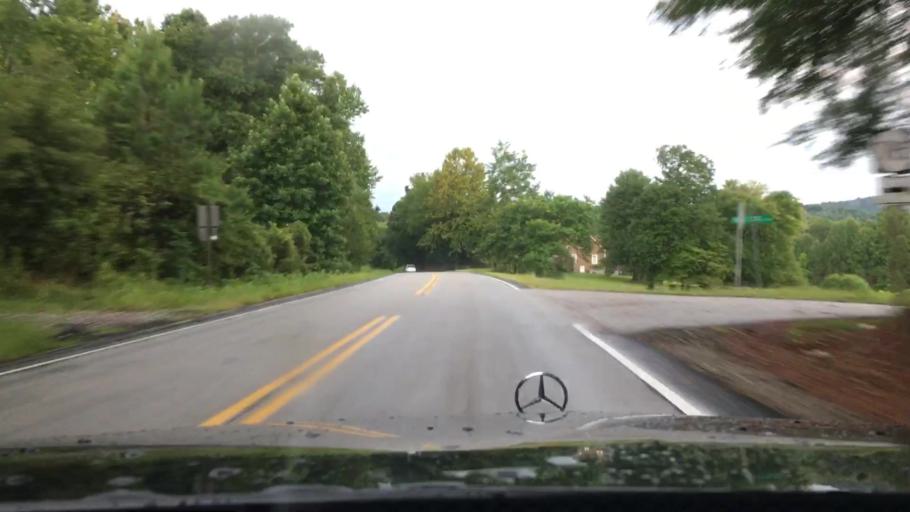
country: US
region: Virginia
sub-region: Amherst County
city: Amherst
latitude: 37.6961
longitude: -79.0296
